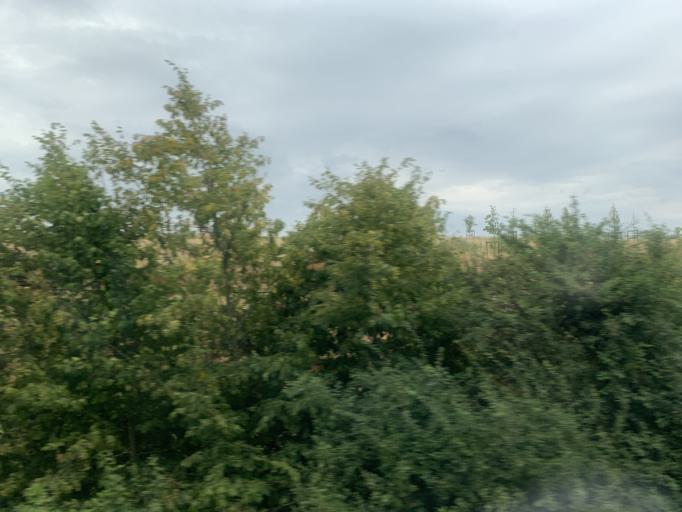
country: DE
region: North Rhine-Westphalia
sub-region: Regierungsbezirk Koln
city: Elsdorf
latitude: 50.8791
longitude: 6.6176
